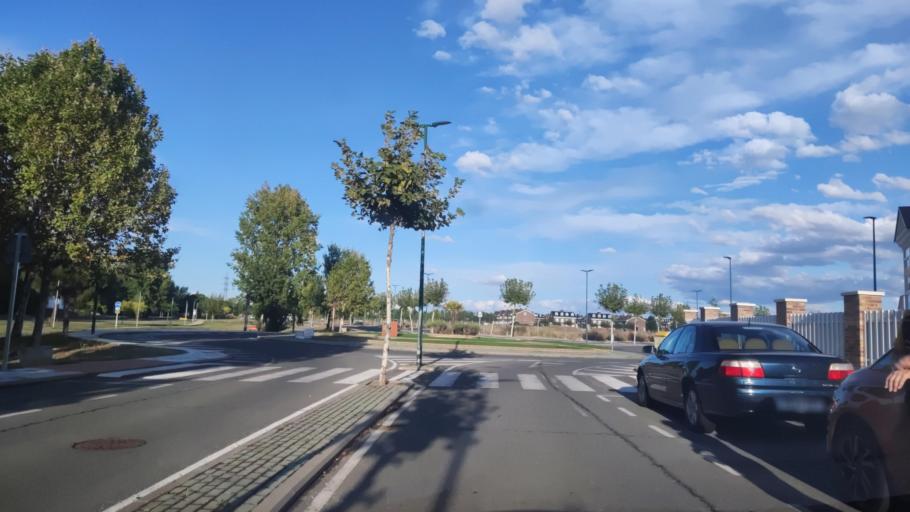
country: ES
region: Castille and Leon
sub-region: Provincia de Salamanca
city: Salamanca
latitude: 40.9557
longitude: -5.6495
